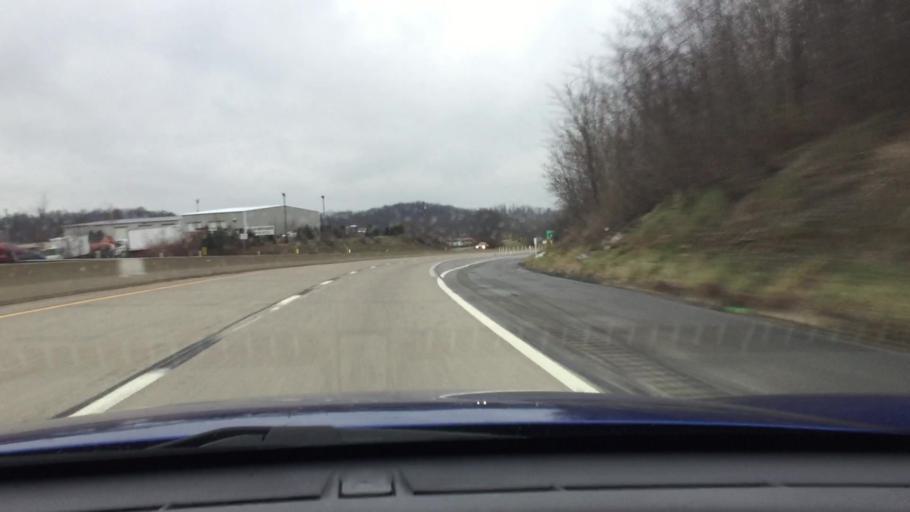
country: US
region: Pennsylvania
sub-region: Allegheny County
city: Imperial
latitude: 40.4312
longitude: -80.2589
